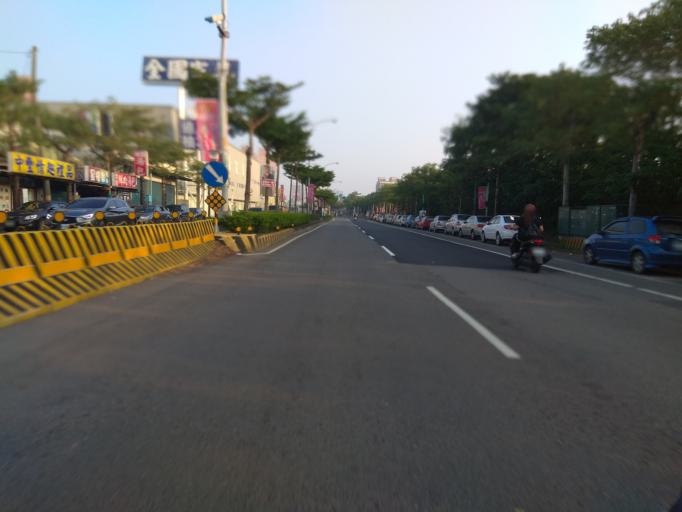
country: TW
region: Taiwan
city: Daxi
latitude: 24.9370
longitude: 121.2160
